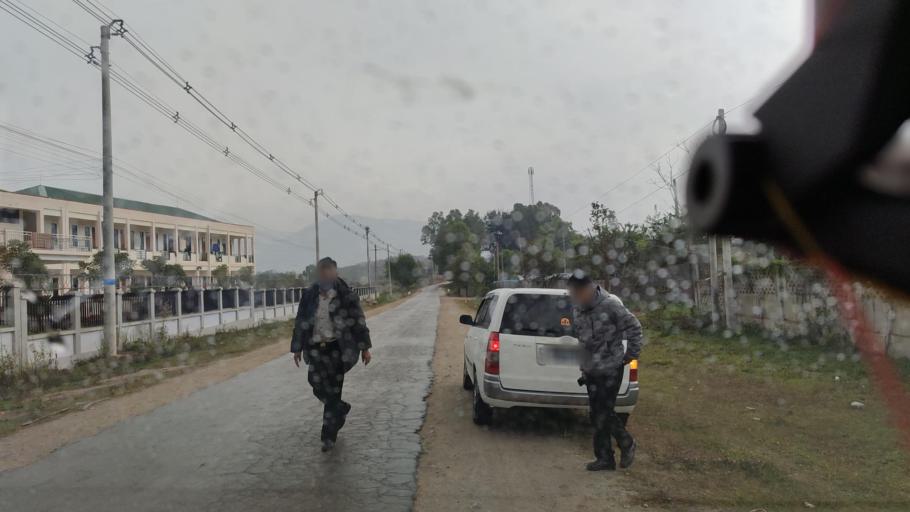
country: TH
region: Chiang Rai
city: Mae Sai
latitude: 21.2607
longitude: 99.6597
